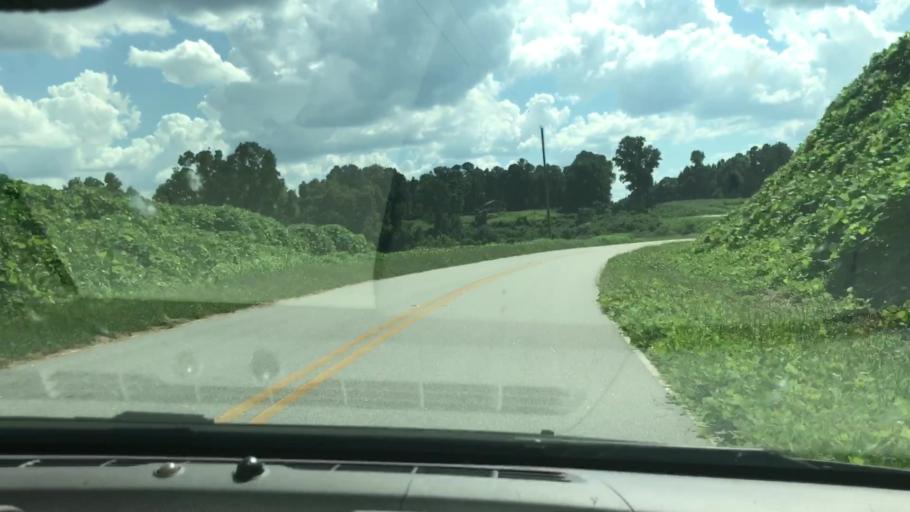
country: US
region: Georgia
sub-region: Troup County
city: La Grange
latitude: 33.0822
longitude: -85.1289
